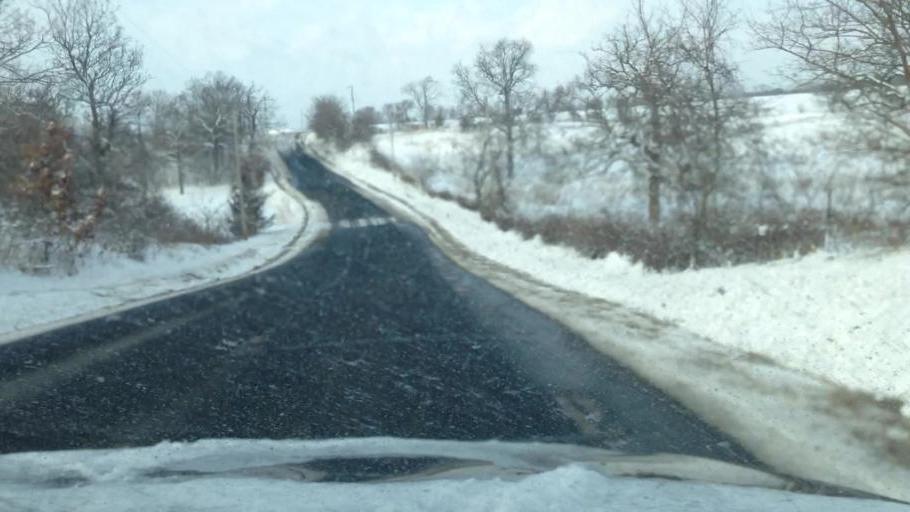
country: US
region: Wisconsin
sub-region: Walworth County
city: East Troy
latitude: 42.7545
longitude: -88.4454
